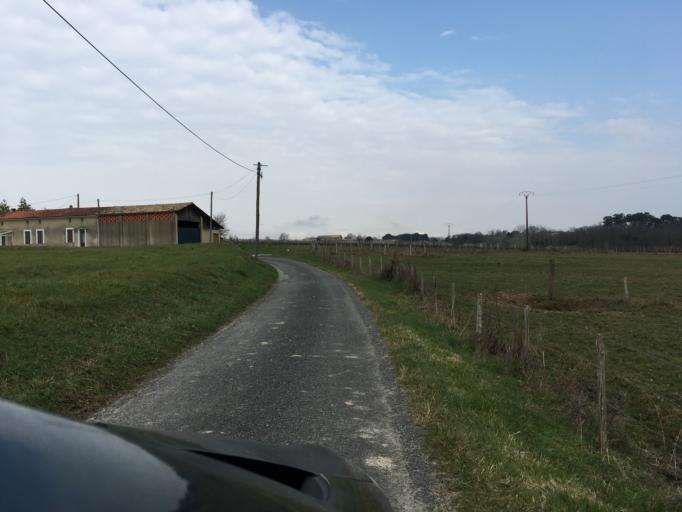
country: FR
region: Poitou-Charentes
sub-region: Departement de la Charente-Maritime
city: Mirambeau
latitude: 45.3333
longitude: -0.5867
